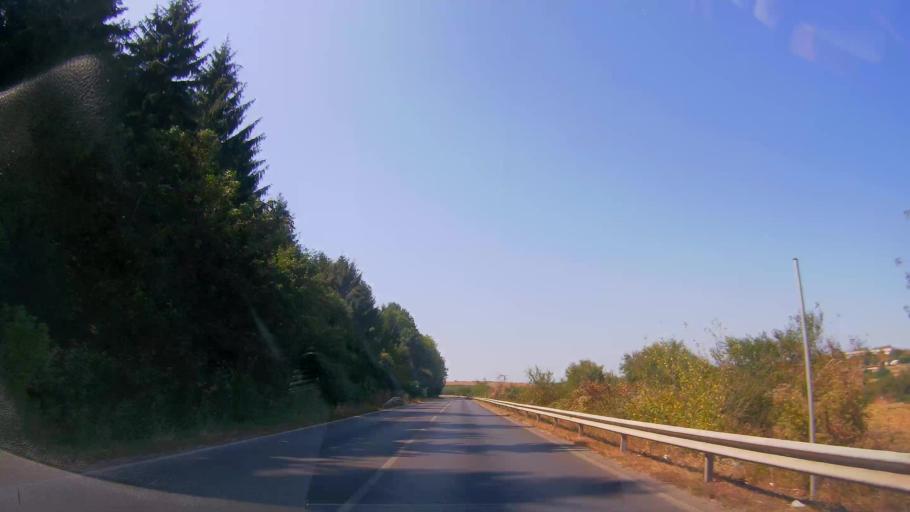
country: BG
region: Razgrad
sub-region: Obshtina Tsar Kaloyan
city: Tsar Kaloyan
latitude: 43.6131
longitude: 26.2277
